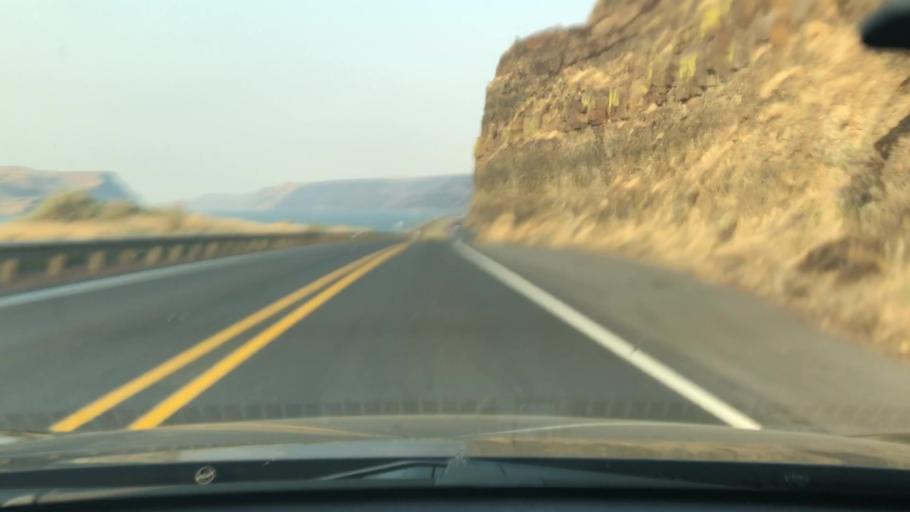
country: US
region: Washington
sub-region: Benton County
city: Highland
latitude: 45.9508
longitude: -119.0585
